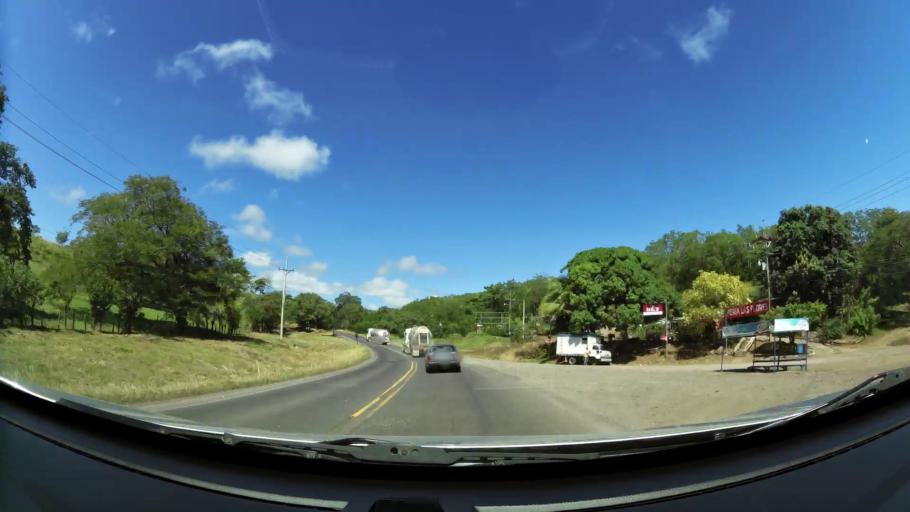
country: CR
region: Guanacaste
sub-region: Canton de Canas
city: Canas
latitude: 10.4011
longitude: -85.0816
